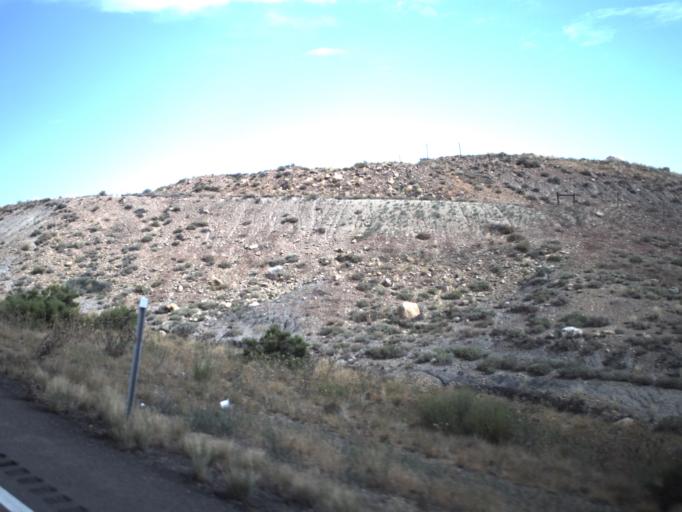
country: US
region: Utah
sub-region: Carbon County
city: East Carbon City
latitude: 39.4997
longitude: -110.5266
